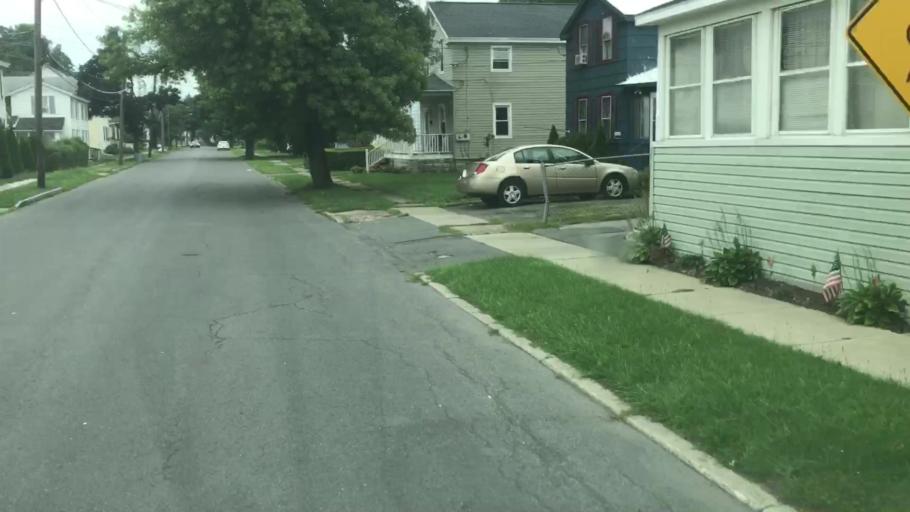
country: US
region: New York
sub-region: Cayuga County
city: Auburn
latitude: 42.9305
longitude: -76.5572
